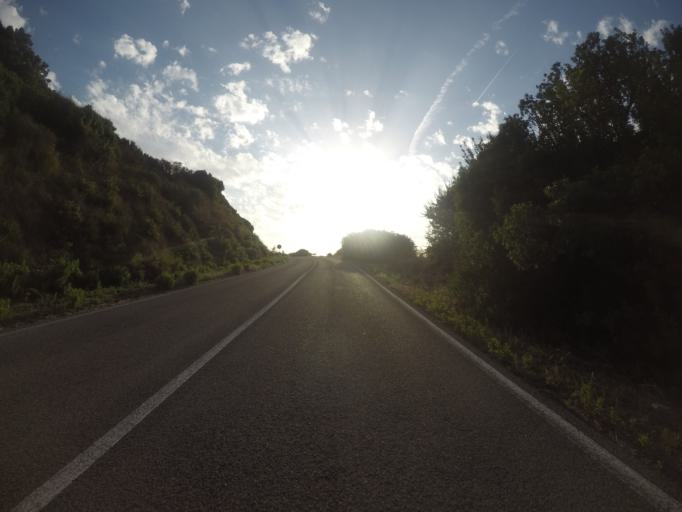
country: IT
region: Sardinia
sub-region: Provincia di Sassari
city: Villanova Monteleone
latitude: 40.4337
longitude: 8.4052
